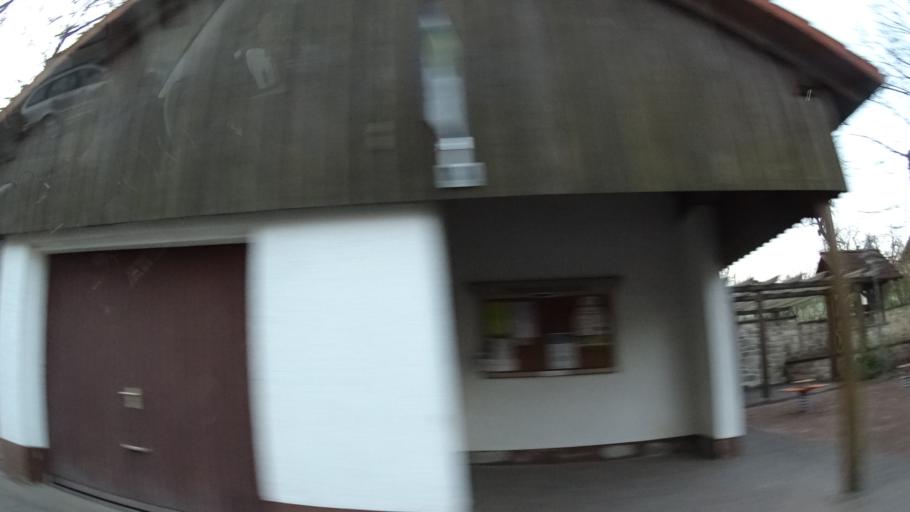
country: DE
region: Rheinland-Pfalz
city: Homberg
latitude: 49.6514
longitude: 7.5154
